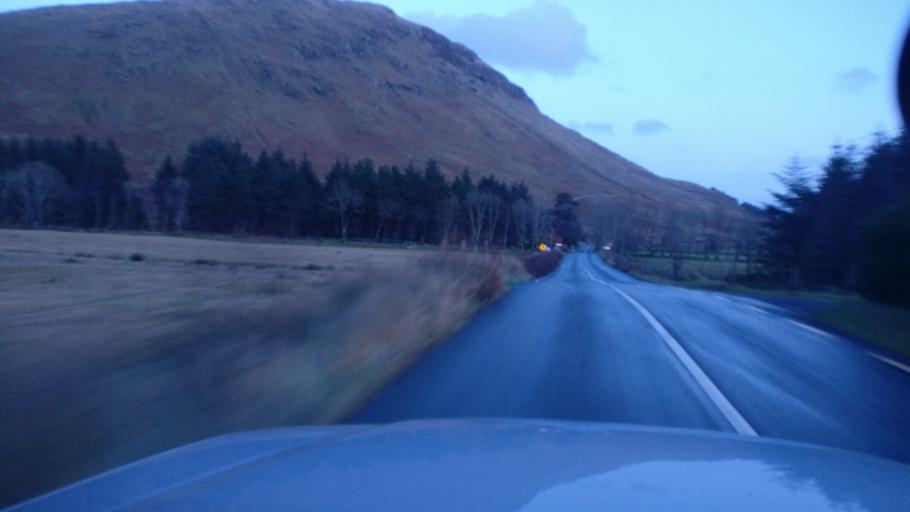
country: IE
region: Connaught
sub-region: Maigh Eo
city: Westport
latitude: 53.5483
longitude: -9.6282
